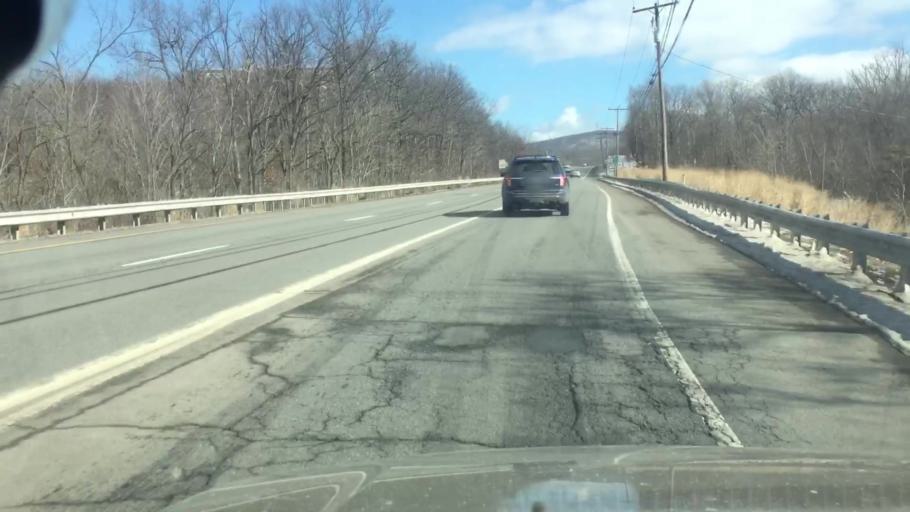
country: US
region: Pennsylvania
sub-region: Luzerne County
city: Hudson
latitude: 41.2502
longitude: -75.8189
